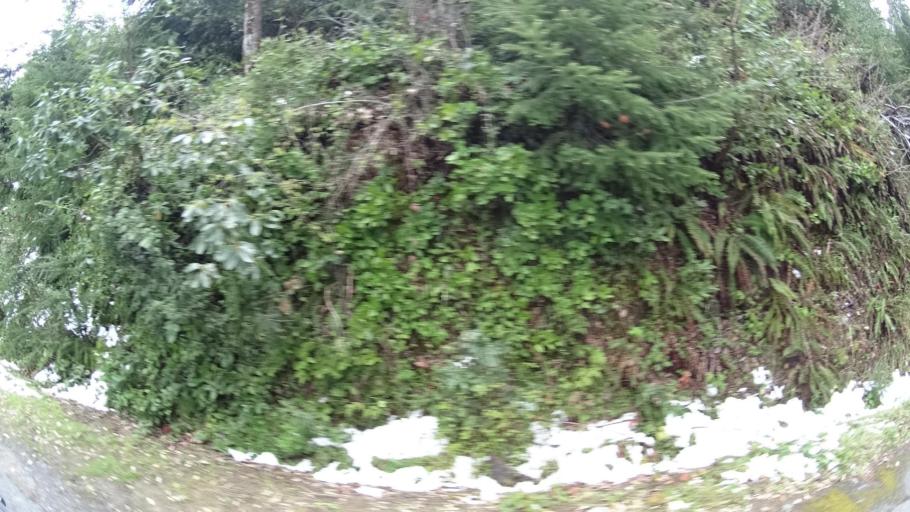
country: US
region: California
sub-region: Humboldt County
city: Blue Lake
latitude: 40.8752
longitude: -123.8839
